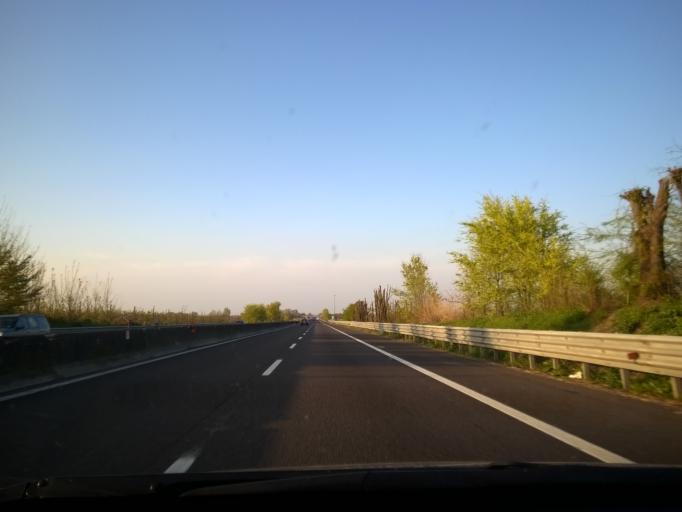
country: IT
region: Emilia-Romagna
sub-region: Provincia di Ferrara
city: Porotto-Cassama
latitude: 44.8222
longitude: 11.5572
